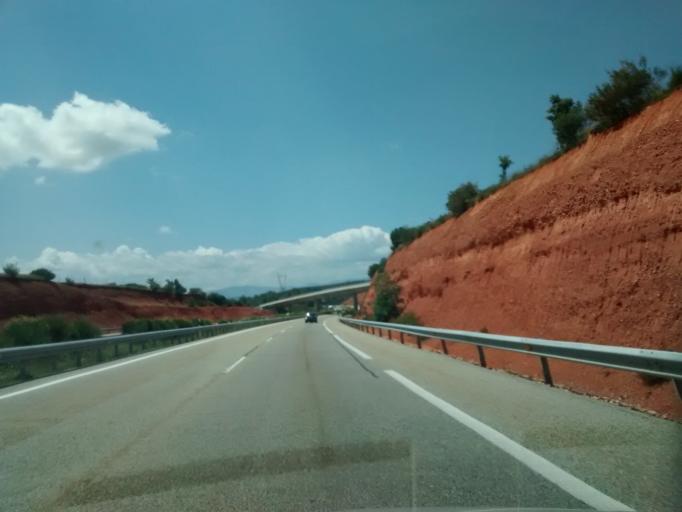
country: ES
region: Castille and Leon
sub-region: Provincia de Leon
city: Brazuelo
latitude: 42.5016
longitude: -6.1208
